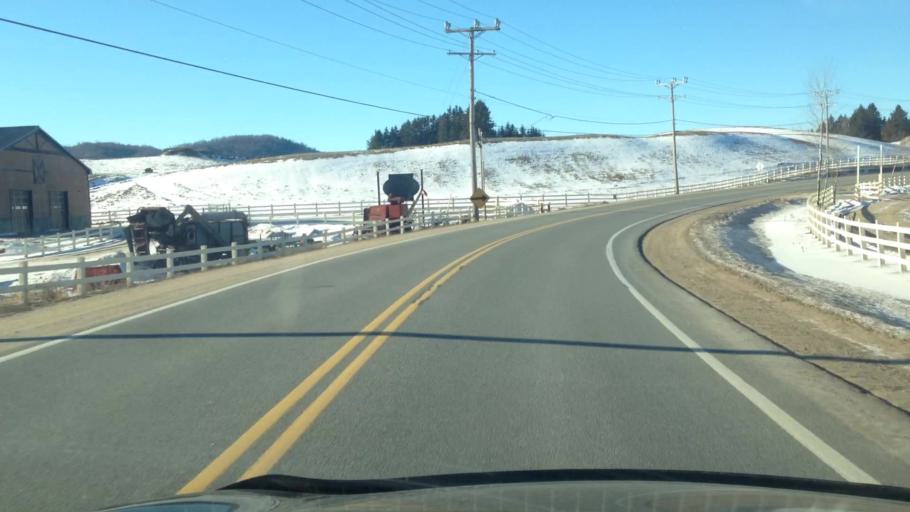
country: CA
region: Quebec
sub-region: Laurentides
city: Mont-Tremblant
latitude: 46.0400
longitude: -74.6041
